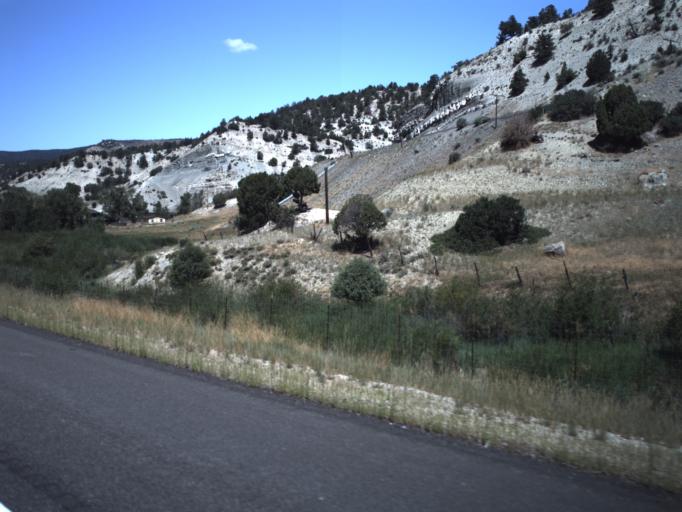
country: US
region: Utah
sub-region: Sanpete County
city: Fairview
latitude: 39.9476
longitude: -111.2127
